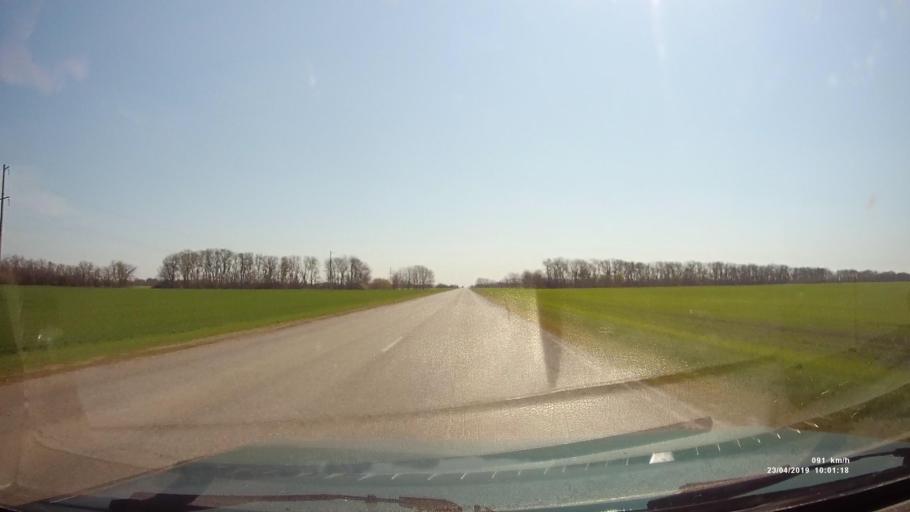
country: RU
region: Rostov
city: Sovetskoye
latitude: 46.7668
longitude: 42.1470
